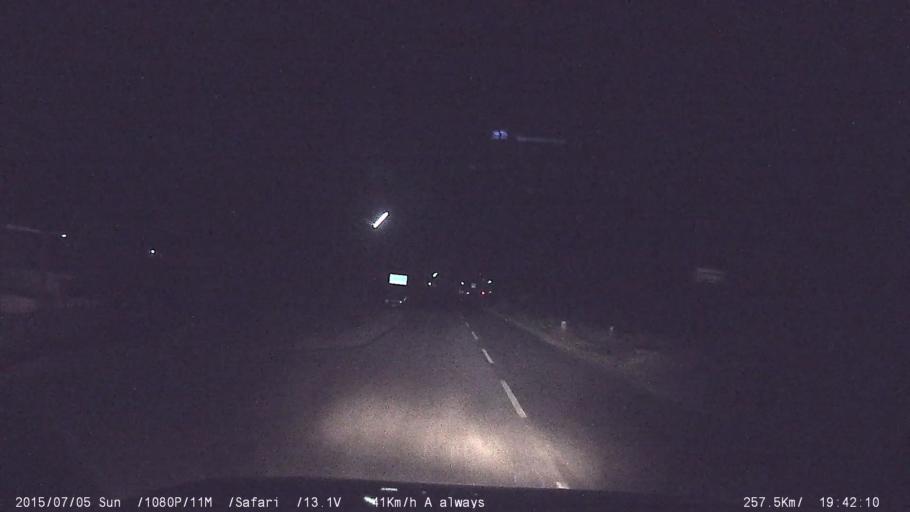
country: IN
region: Kerala
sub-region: Palakkad district
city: Palakkad
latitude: 10.7592
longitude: 76.5511
